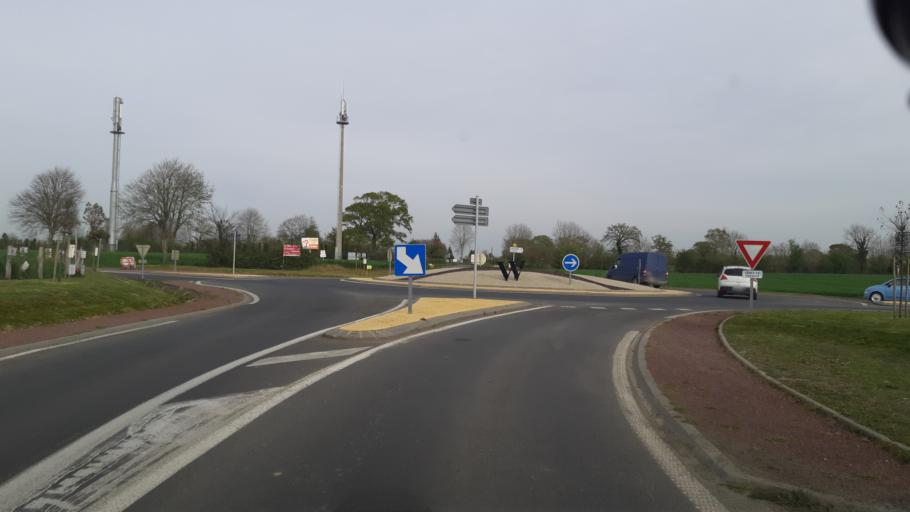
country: FR
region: Lower Normandy
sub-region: Departement de la Manche
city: Brehal
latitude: 48.8960
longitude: -1.5027
